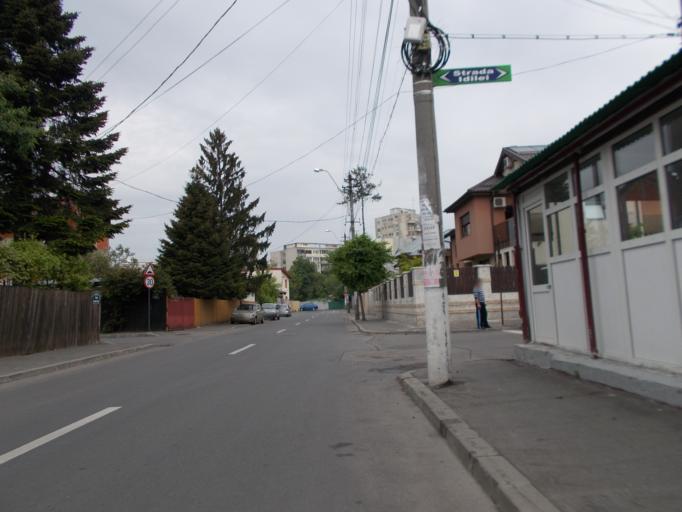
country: RO
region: Bucuresti
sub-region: Municipiul Bucuresti
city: Bucuresti
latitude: 44.3889
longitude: 26.0956
